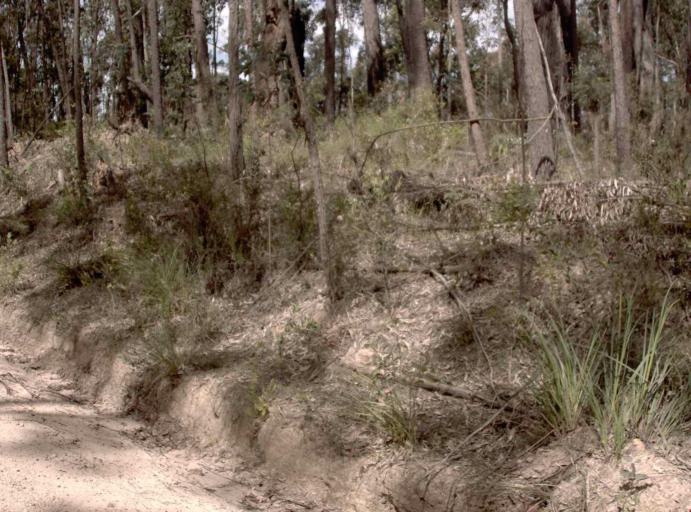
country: AU
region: Victoria
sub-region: East Gippsland
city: Lakes Entrance
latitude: -37.6544
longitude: 148.6520
